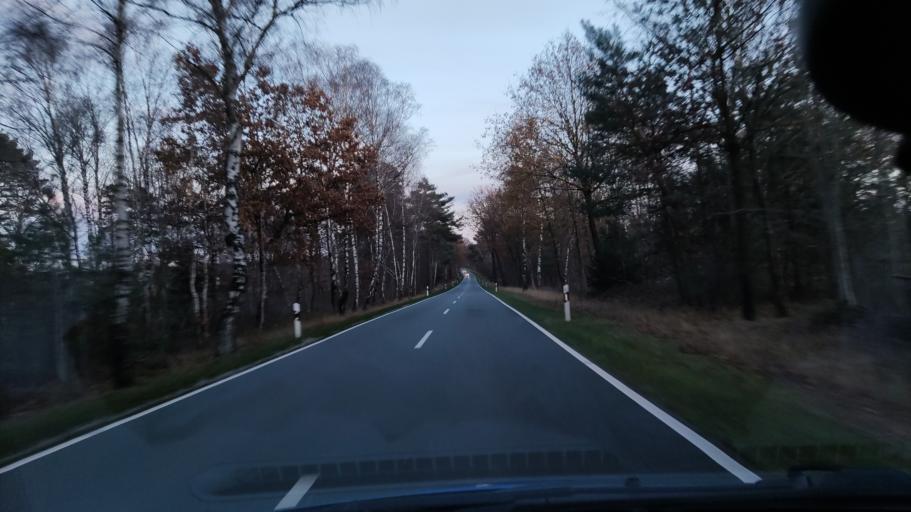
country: DE
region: Lower Saxony
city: Schneverdingen
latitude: 53.1257
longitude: 9.8337
